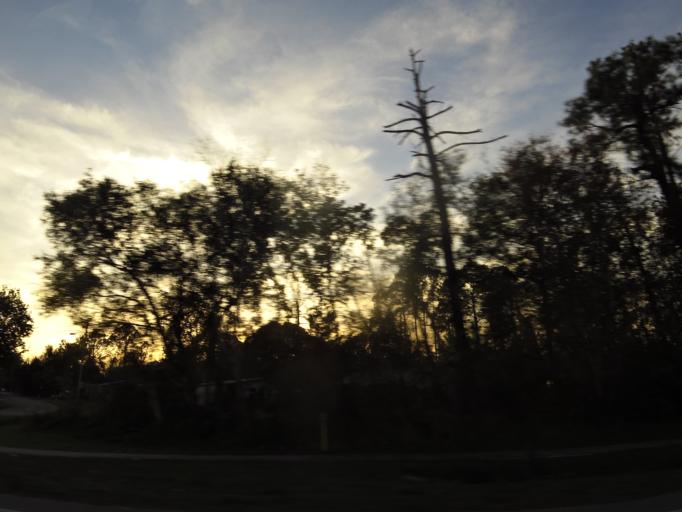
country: US
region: Florida
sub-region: Volusia County
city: North DeLand
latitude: 29.0808
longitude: -81.3049
